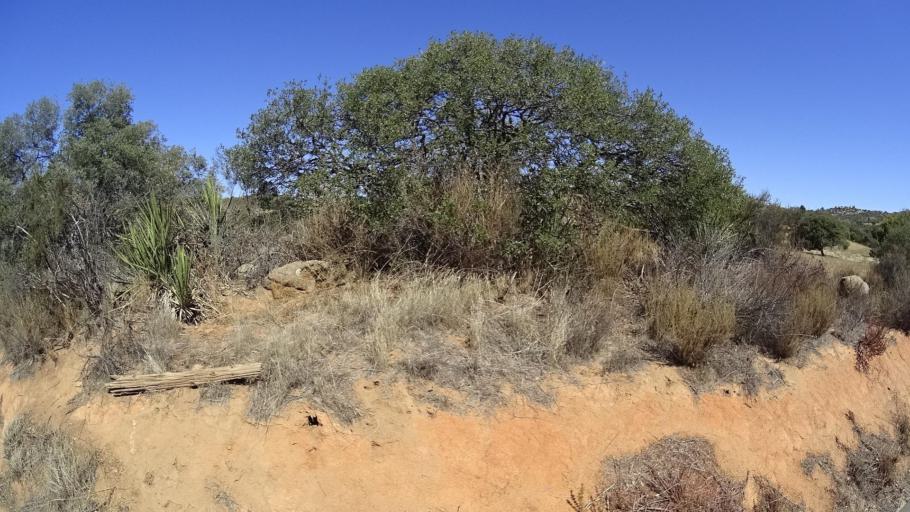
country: US
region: California
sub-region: San Diego County
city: Alpine
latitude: 32.7684
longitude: -116.6858
